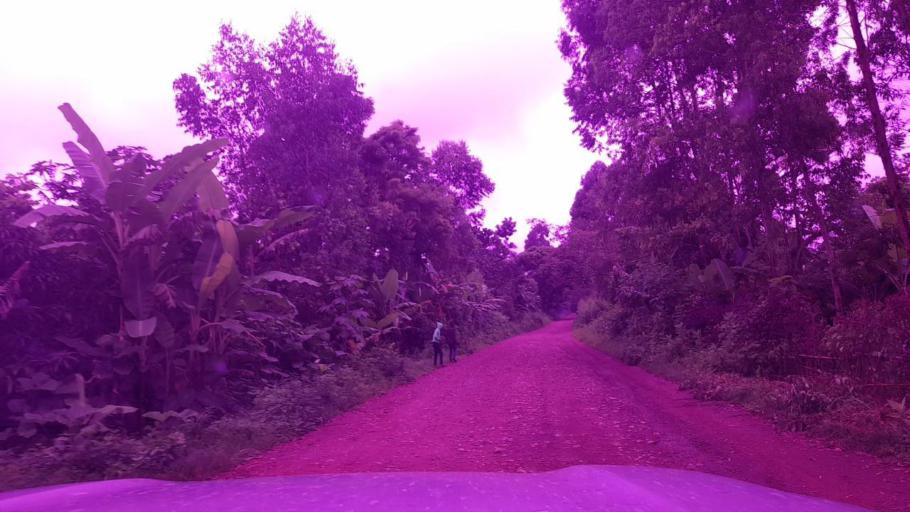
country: ET
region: Southern Nations, Nationalities, and People's Region
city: Bonga
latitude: 7.5763
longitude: 36.0241
